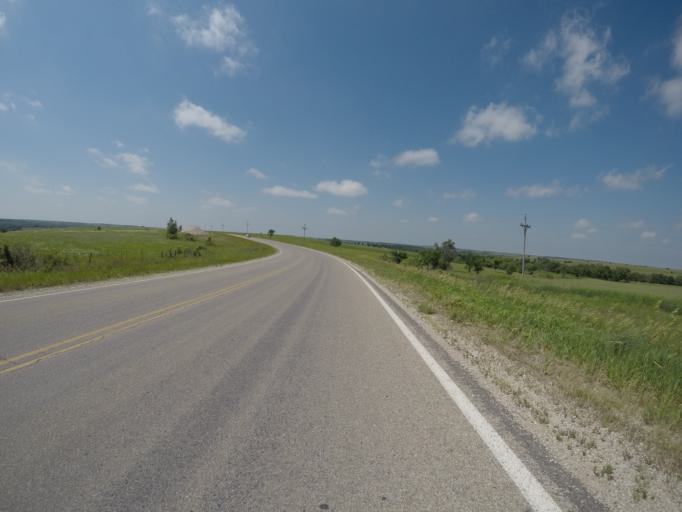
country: US
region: Kansas
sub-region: Pottawatomie County
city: Westmoreland
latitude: 39.3910
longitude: -96.4259
